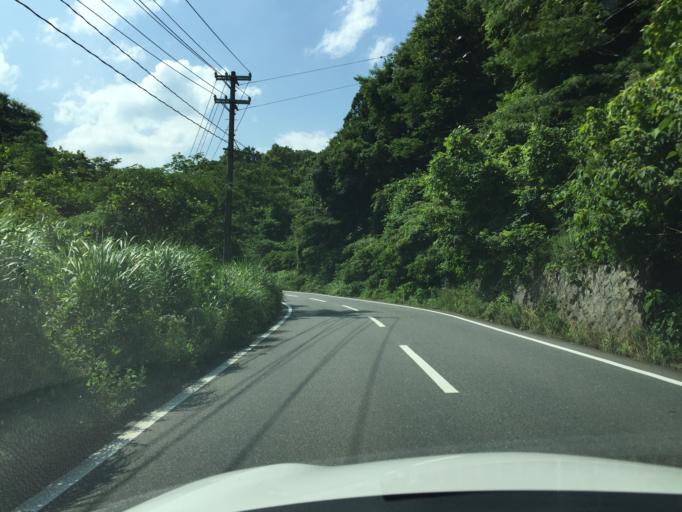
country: JP
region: Ibaraki
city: Kitaibaraki
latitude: 36.9113
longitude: 140.7474
